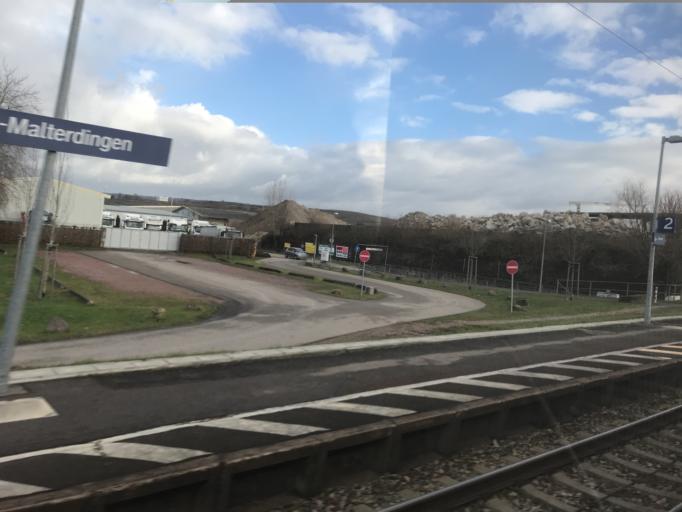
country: DE
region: Baden-Wuerttemberg
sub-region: Freiburg Region
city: Riegel
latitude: 48.1516
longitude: 7.7712
